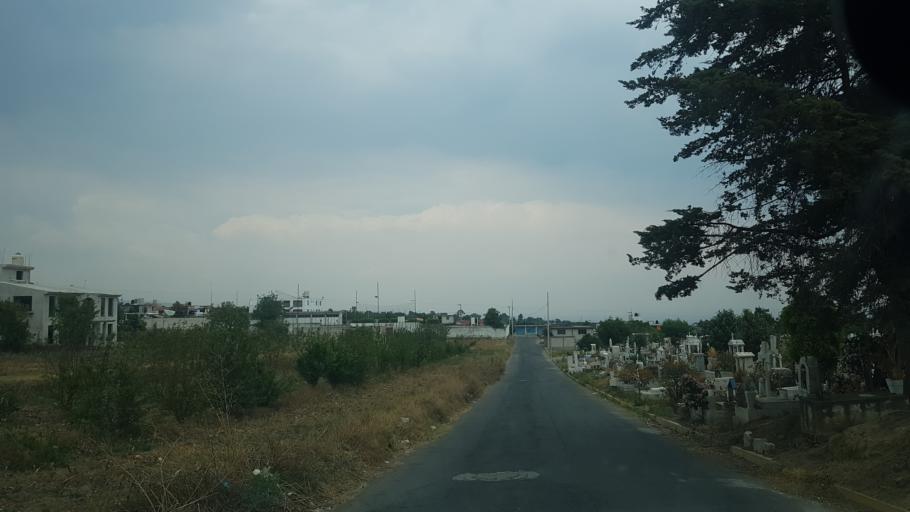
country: MX
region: Puebla
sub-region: Chiautzingo
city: San Nicolas Zecalacoayan
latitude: 19.1739
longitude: -98.4915
